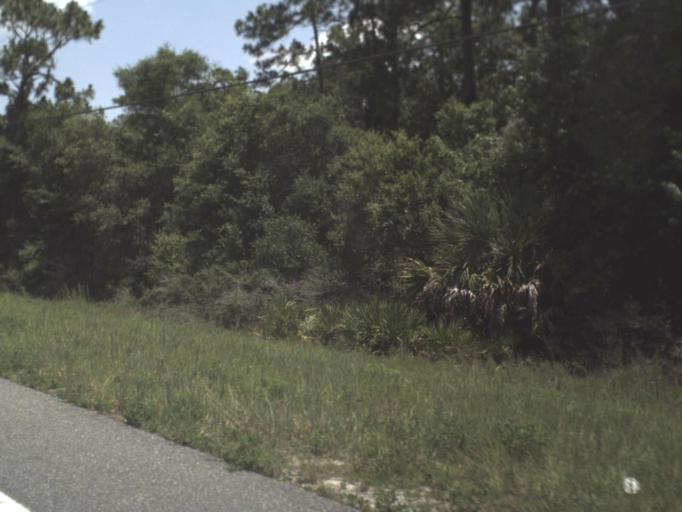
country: US
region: Florida
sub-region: Taylor County
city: Steinhatchee
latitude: 29.7024
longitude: -83.3577
